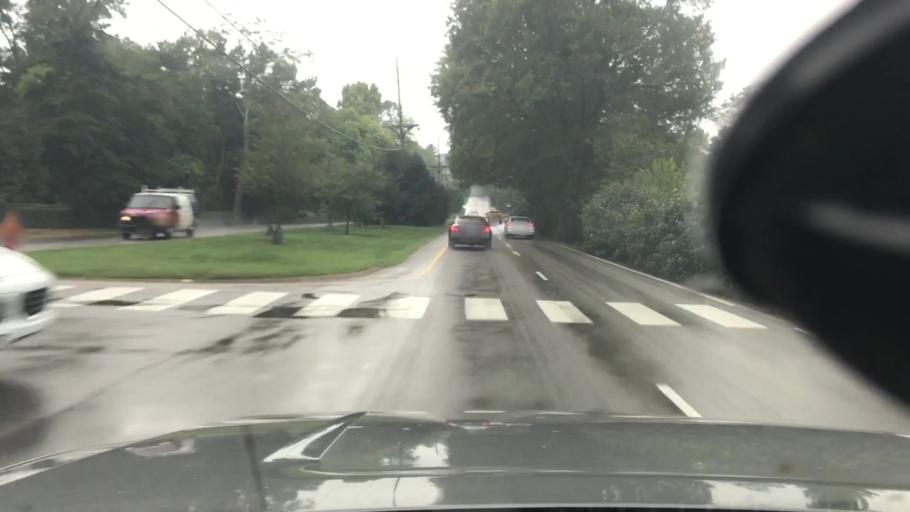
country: US
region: Tennessee
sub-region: Davidson County
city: Belle Meade
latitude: 36.0907
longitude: -86.8600
